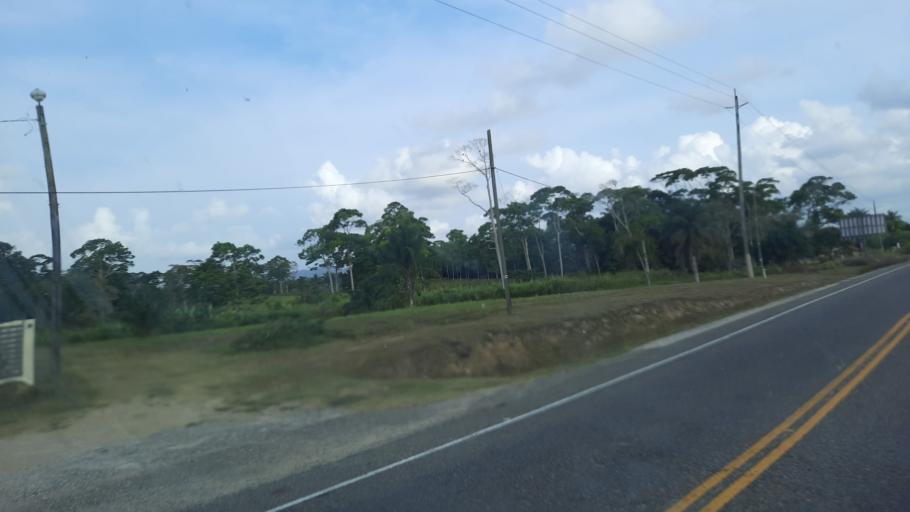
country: BZ
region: Stann Creek
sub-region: Dangriga
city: Dangriga
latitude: 16.9857
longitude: -88.2973
